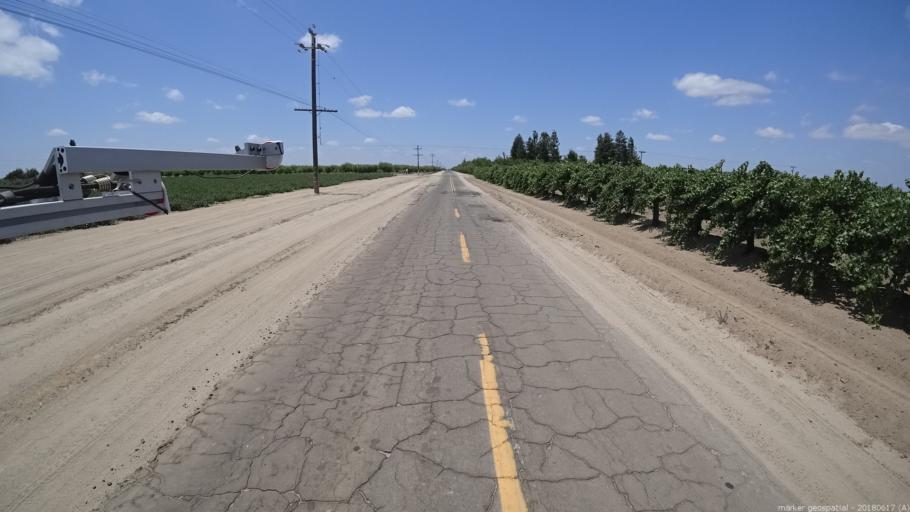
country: US
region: California
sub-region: Fresno County
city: Kerman
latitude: 36.8223
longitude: -120.1500
